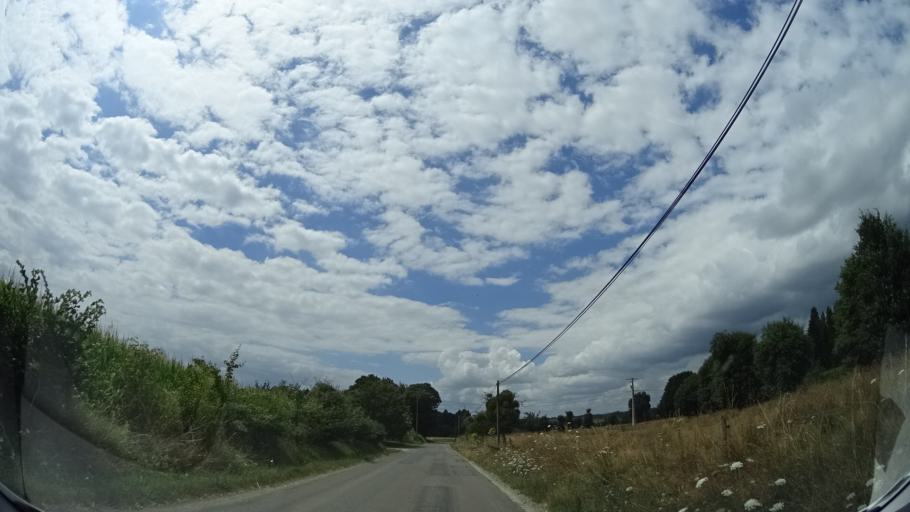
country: FR
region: Brittany
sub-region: Departement d'Ille-et-Vilaine
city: La Meziere
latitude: 48.1953
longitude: -1.7592
